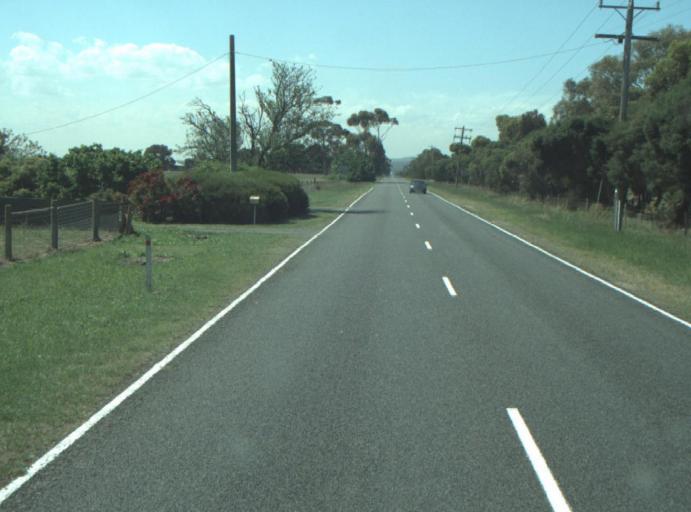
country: AU
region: Victoria
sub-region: Greater Geelong
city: Lara
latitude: -38.0061
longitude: 144.3993
